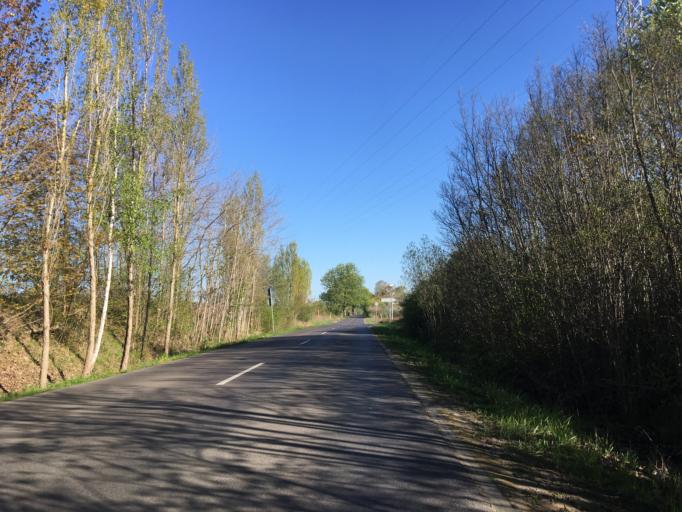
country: DE
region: Brandenburg
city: Bernau bei Berlin
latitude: 52.6828
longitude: 13.5538
